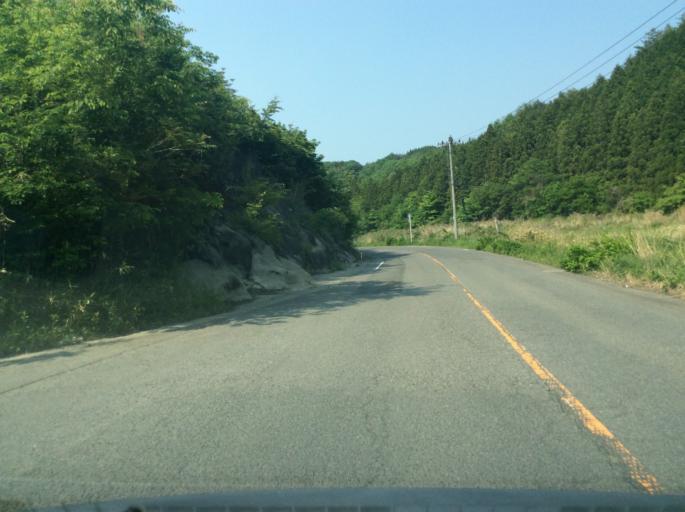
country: JP
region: Tochigi
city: Kuroiso
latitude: 37.0787
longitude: 140.2222
